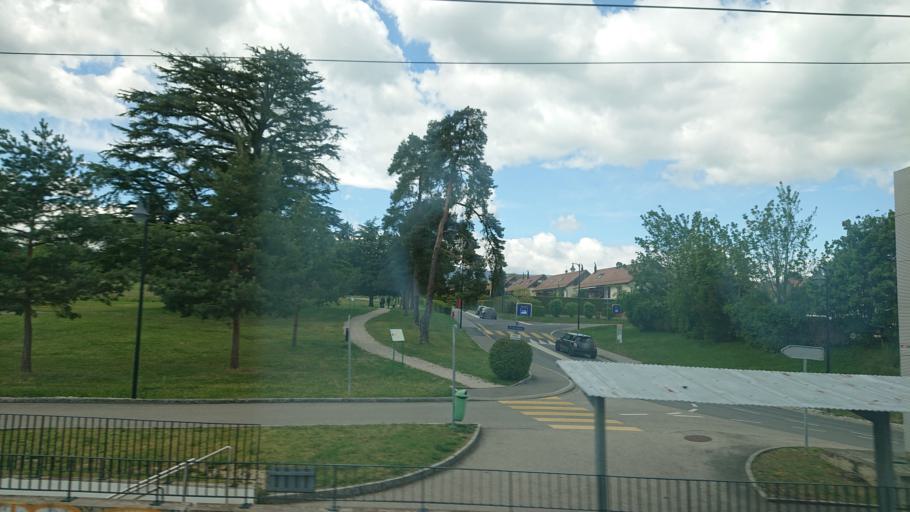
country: CH
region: Vaud
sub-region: Nyon District
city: Coppet
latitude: 46.3076
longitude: 6.1808
